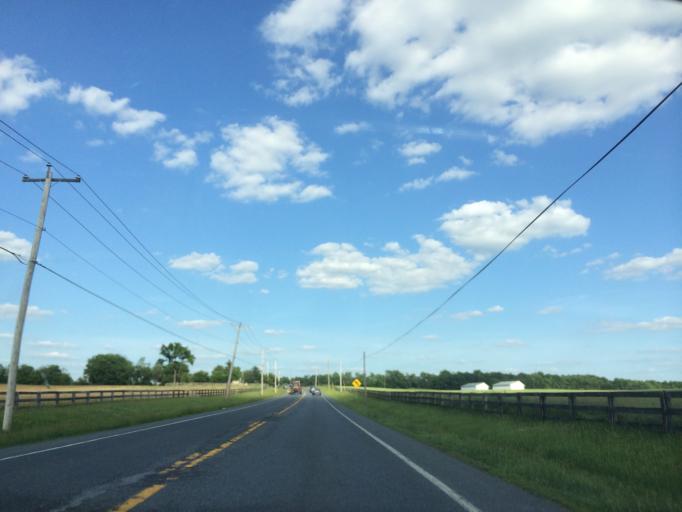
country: US
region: Maryland
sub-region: Frederick County
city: Walkersville
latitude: 39.4523
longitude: -77.3506
